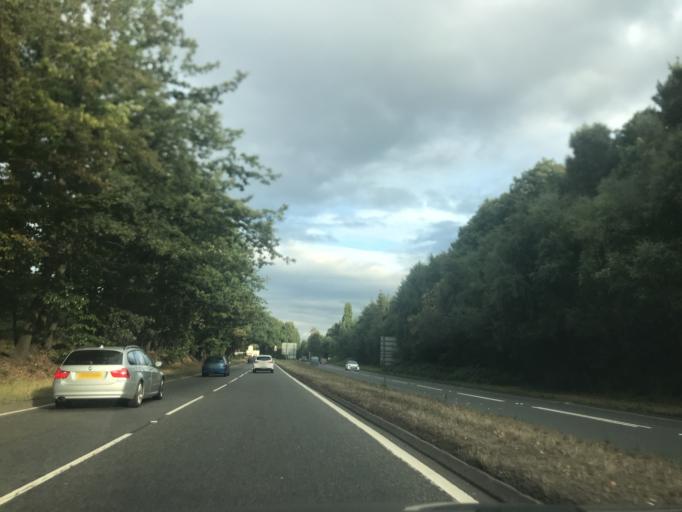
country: GB
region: England
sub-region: Surrey
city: Bagshot
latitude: 51.3757
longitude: -0.6995
